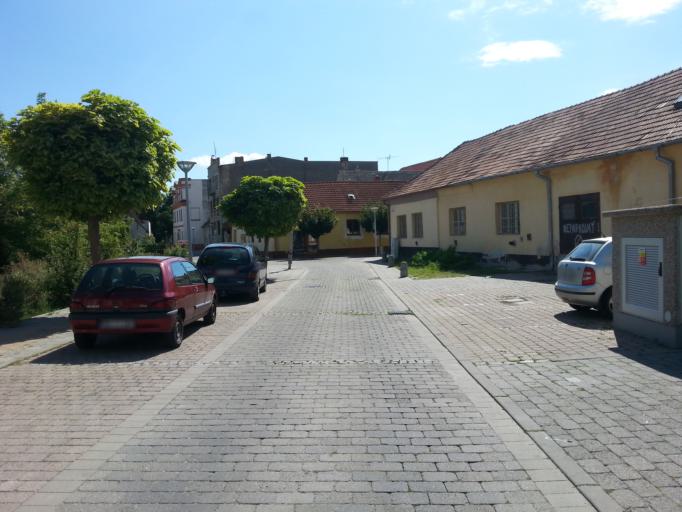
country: SK
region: Trenciansky
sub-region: Okres Nove Mesto nad Vahom
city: Nove Mesto nad Vahom
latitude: 48.7588
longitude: 17.8324
